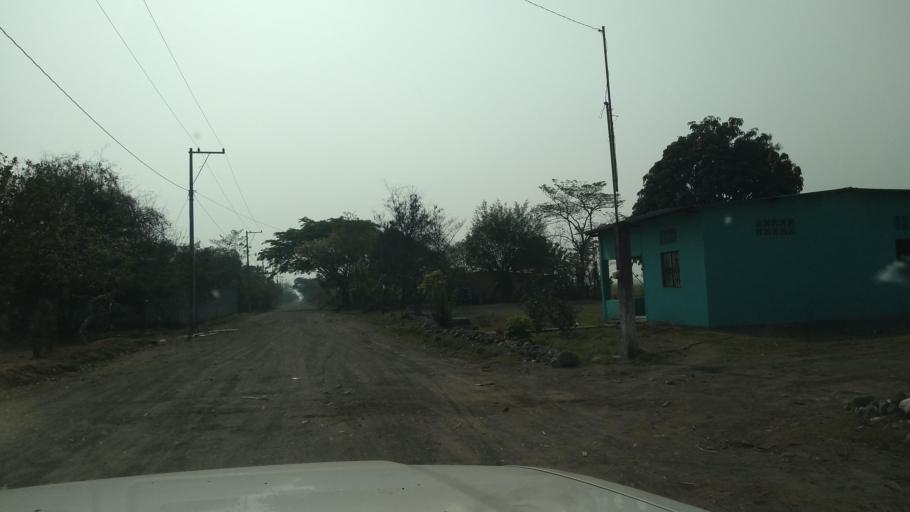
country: MX
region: Oaxaca
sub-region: Cosolapa
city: Cosolapa
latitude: 18.6224
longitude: -96.6056
